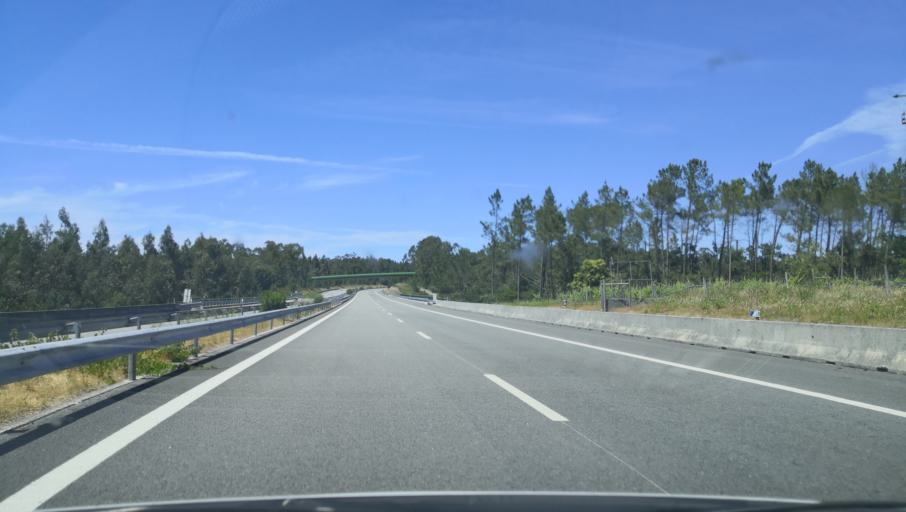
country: PT
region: Coimbra
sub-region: Montemor-O-Velho
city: Montemor-o-Velho
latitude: 40.2135
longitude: -8.6749
